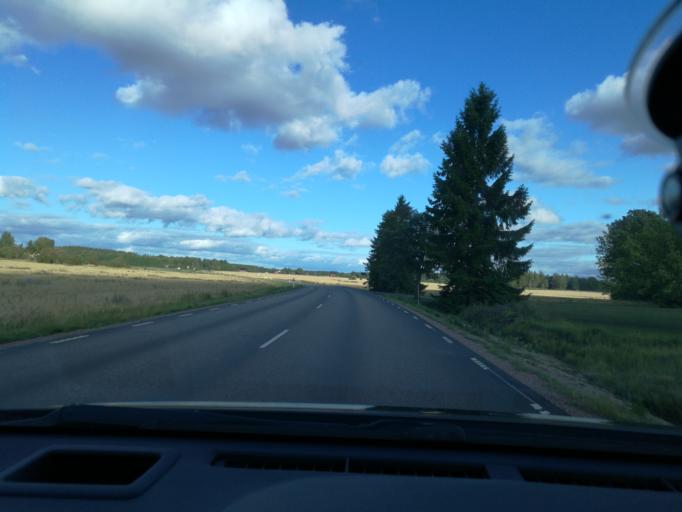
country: SE
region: Vaestmanland
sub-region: Hallstahammars Kommun
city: Kolback
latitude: 59.5629
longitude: 16.2890
